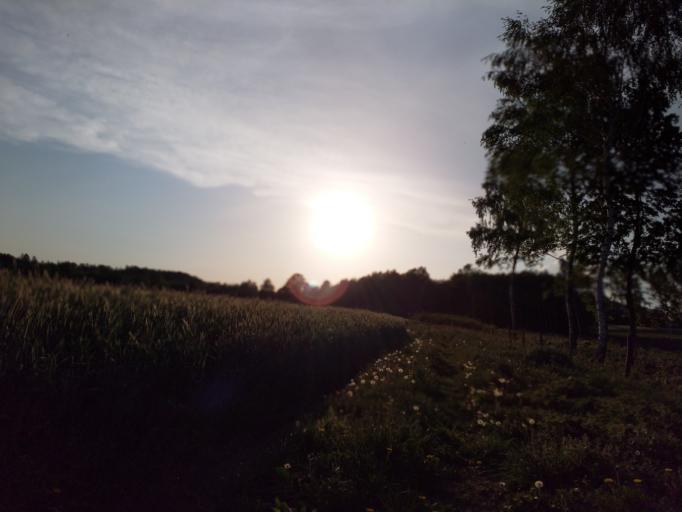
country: LV
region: Aizpute
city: Aizpute
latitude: 56.8287
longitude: 21.7835
